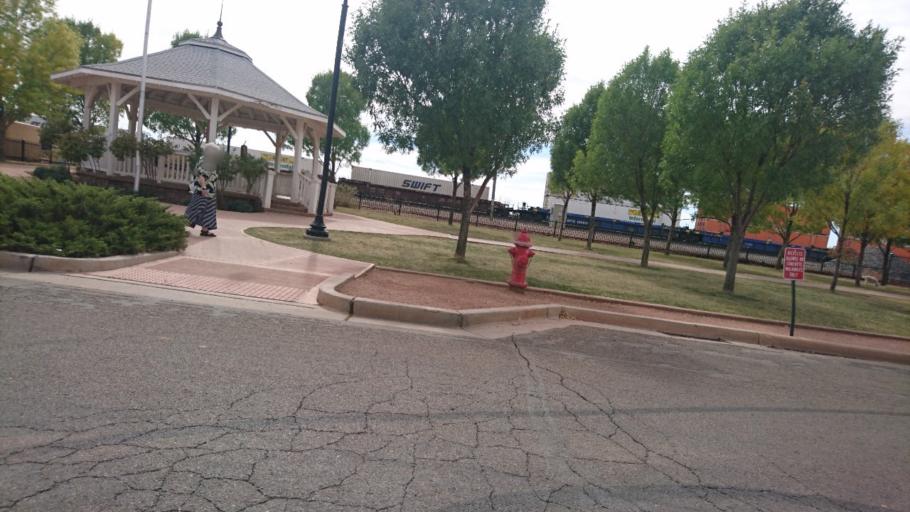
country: US
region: Arizona
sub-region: Navajo County
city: Winslow
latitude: 35.0226
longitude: -110.6986
